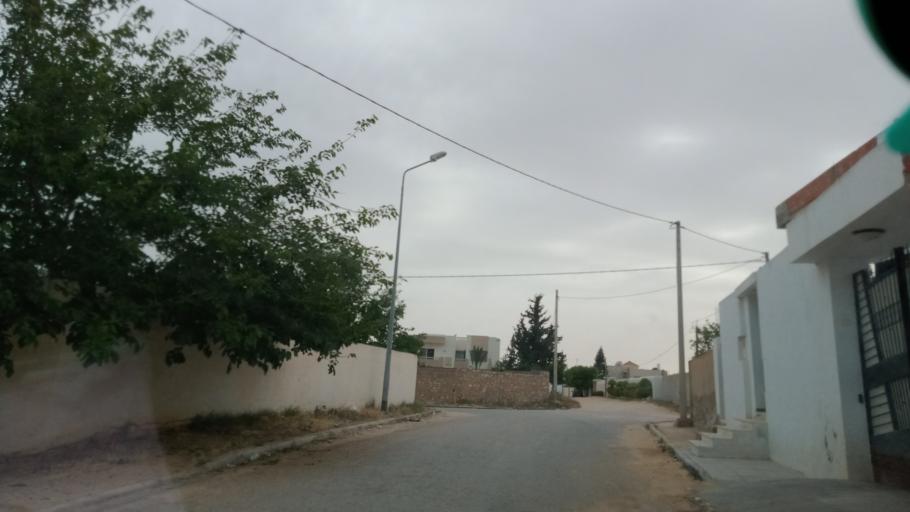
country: TN
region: Safaqis
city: Al Qarmadah
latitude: 34.7997
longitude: 10.7521
